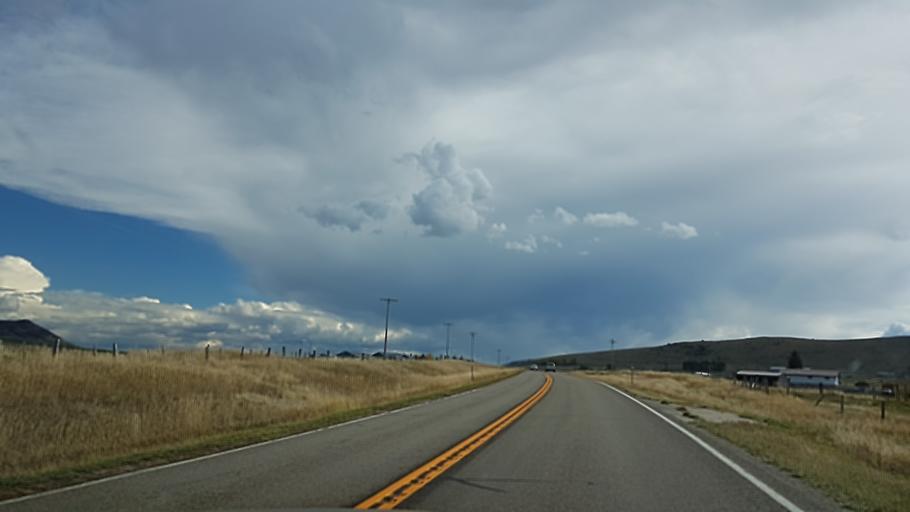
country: US
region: Montana
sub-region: Jefferson County
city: Whitehall
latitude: 45.7884
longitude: -111.9185
